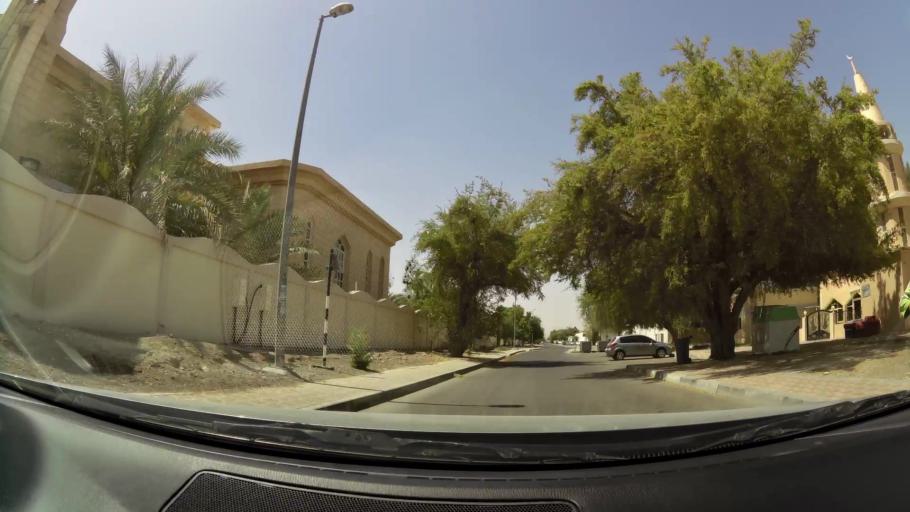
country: OM
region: Al Buraimi
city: Al Buraymi
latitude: 24.2814
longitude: 55.7762
